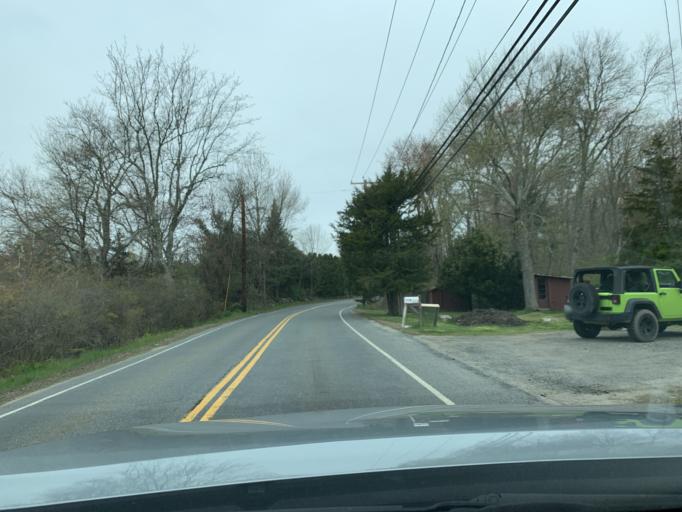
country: US
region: Rhode Island
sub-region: Washington County
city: North Kingstown
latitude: 41.5914
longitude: -71.4824
